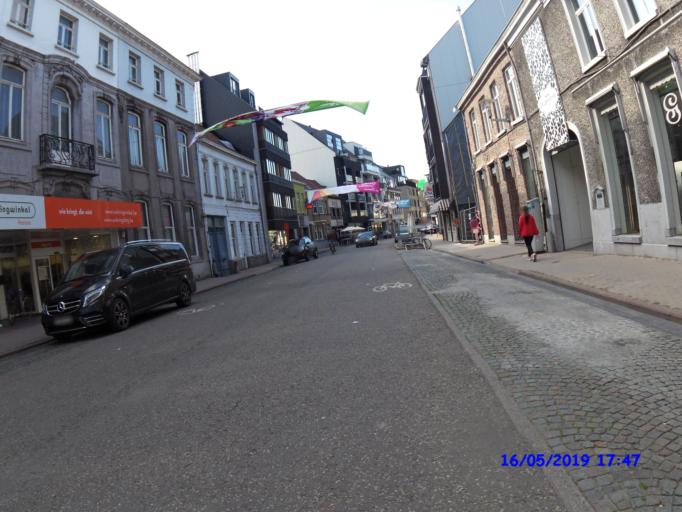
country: BE
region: Flanders
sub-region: Provincie Oost-Vlaanderen
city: Deinze
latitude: 50.9798
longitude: 3.5303
